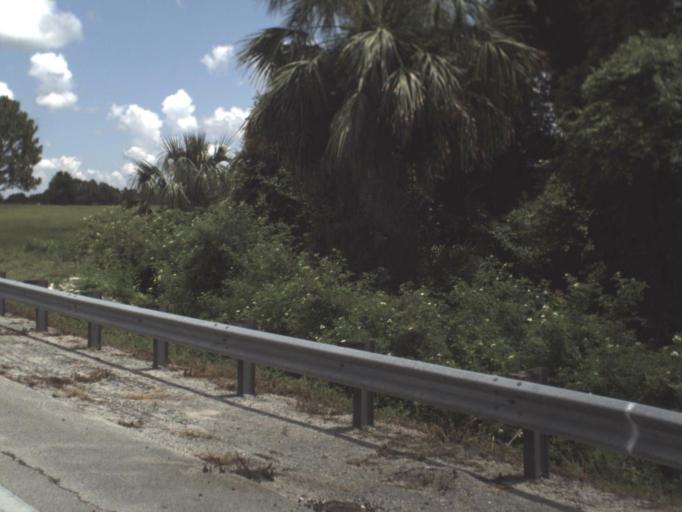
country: US
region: Florida
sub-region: Putnam County
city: Palatka
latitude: 29.5419
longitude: -81.6487
